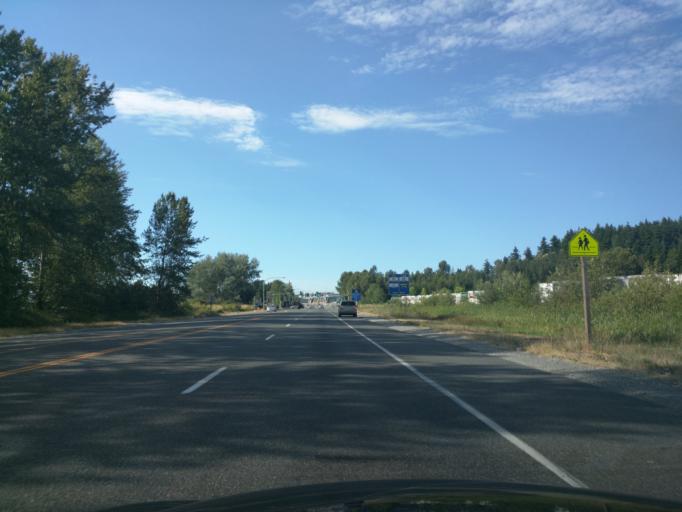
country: US
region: Washington
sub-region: Whatcom County
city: Blaine
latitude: 48.9919
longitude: -122.7349
